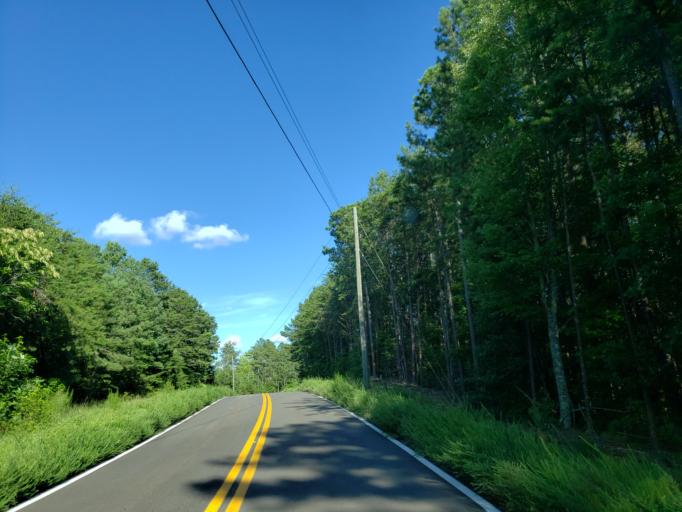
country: US
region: Georgia
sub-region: Bartow County
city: Rydal
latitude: 34.3630
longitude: -84.6184
